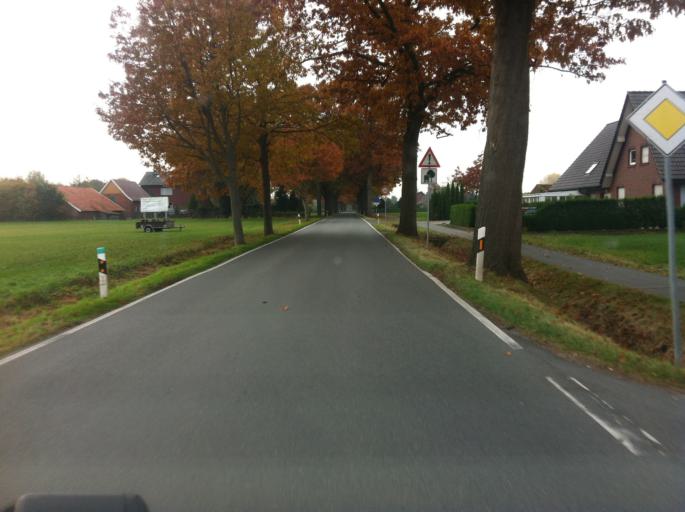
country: DE
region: North Rhine-Westphalia
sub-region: Regierungsbezirk Munster
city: Vreden
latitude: 52.0166
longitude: 6.7983
